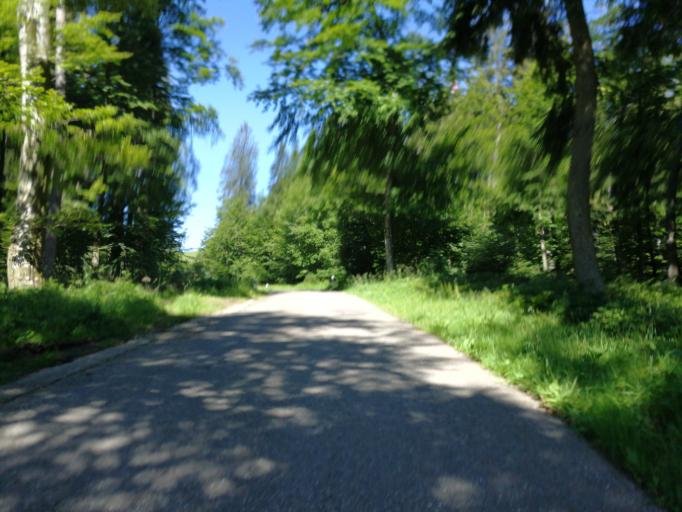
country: CH
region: Zurich
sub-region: Bezirk Hinwil
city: Wald
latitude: 47.2937
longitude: 8.8900
